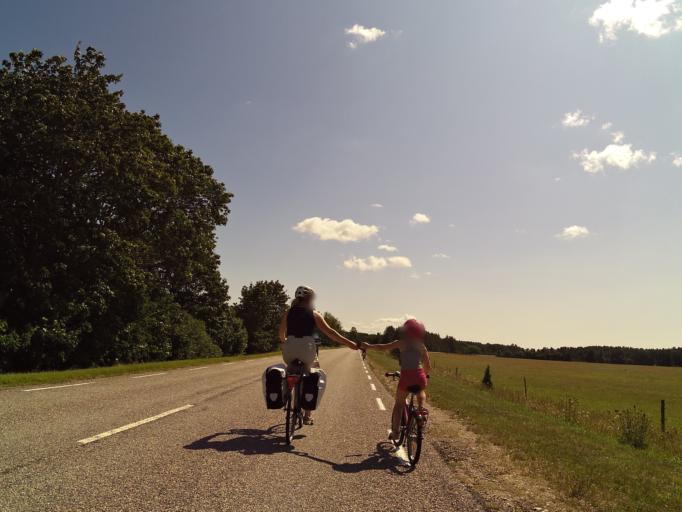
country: EE
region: Hiiumaa
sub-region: Kaerdla linn
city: Kardla
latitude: 58.7349
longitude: 22.6266
